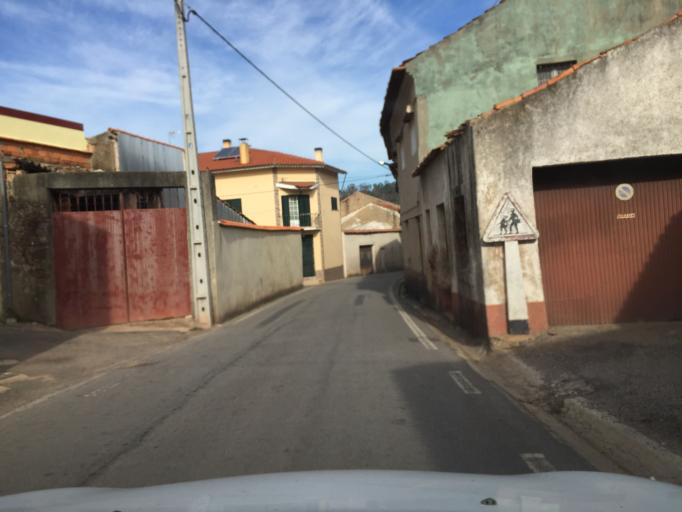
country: PT
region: Aveiro
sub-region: Anadia
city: Anadia
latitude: 40.4089
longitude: -8.3988
